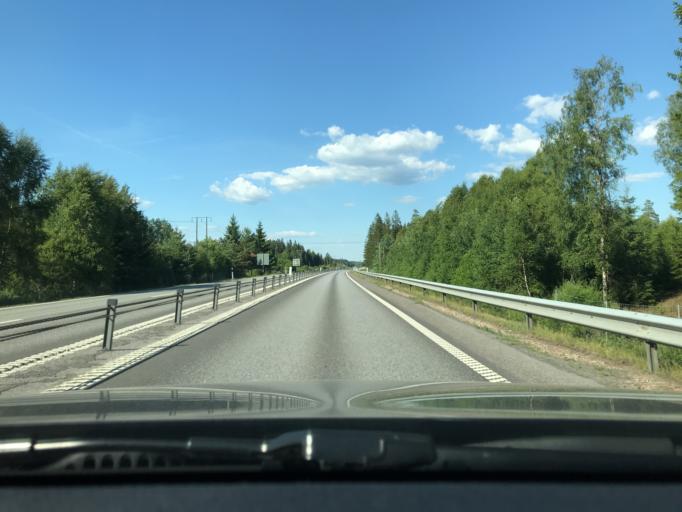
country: SE
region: Skane
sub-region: Osby Kommun
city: Osby
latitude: 56.4379
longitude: 14.0662
